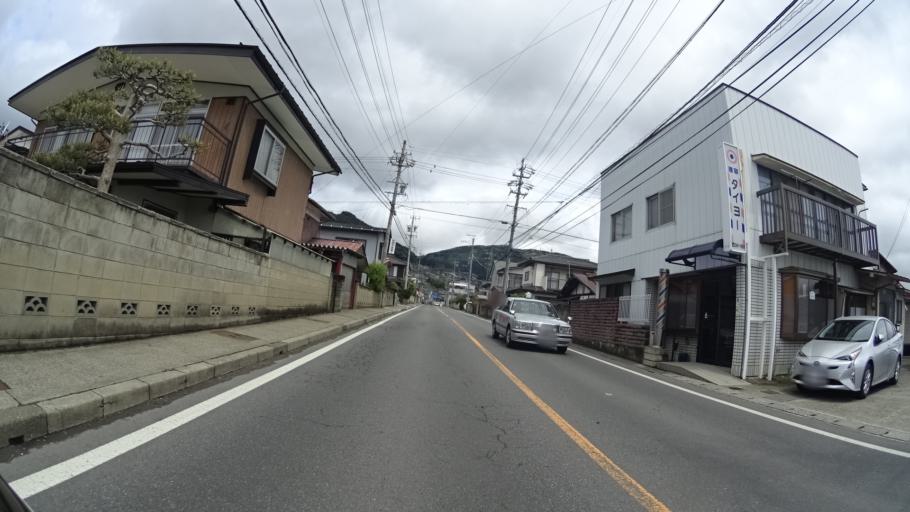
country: JP
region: Nagano
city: Nagano-shi
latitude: 36.6786
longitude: 138.2005
